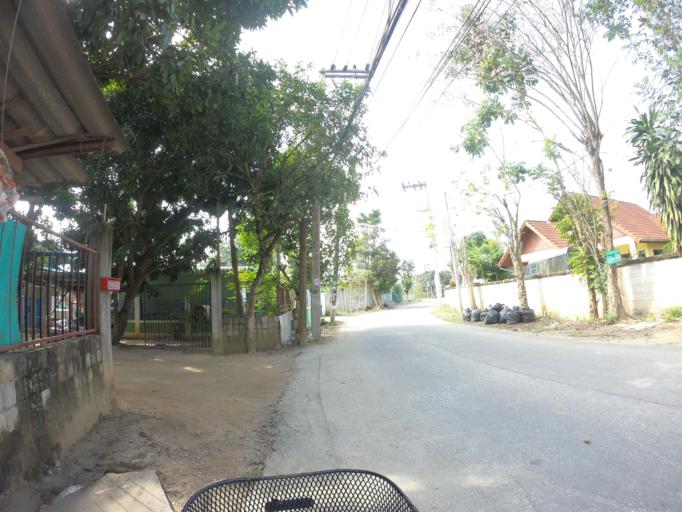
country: TH
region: Chiang Mai
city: Saraphi
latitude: 18.7259
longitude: 99.0626
